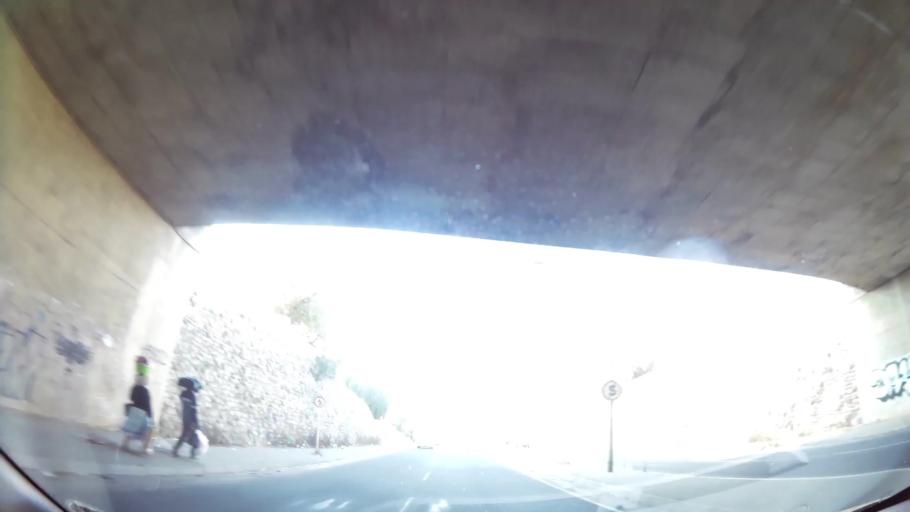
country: ZA
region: Gauteng
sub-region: City of Johannesburg Metropolitan Municipality
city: Roodepoort
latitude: -26.1370
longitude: 27.8622
